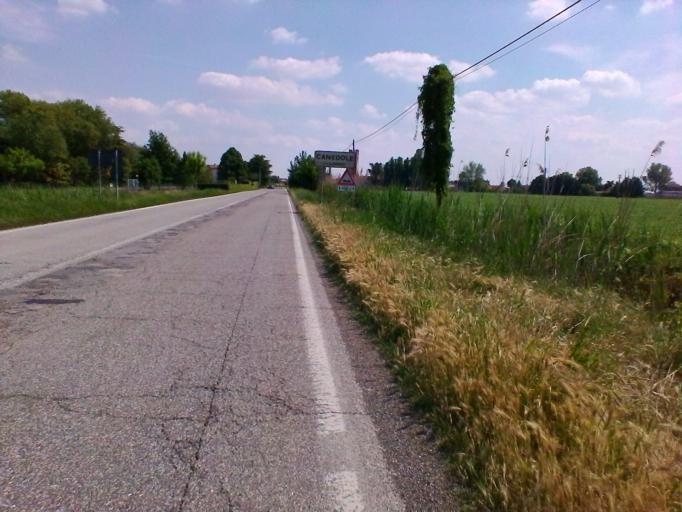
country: IT
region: Veneto
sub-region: Provincia di Verona
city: Pradelle
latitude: 45.2392
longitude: 10.8403
